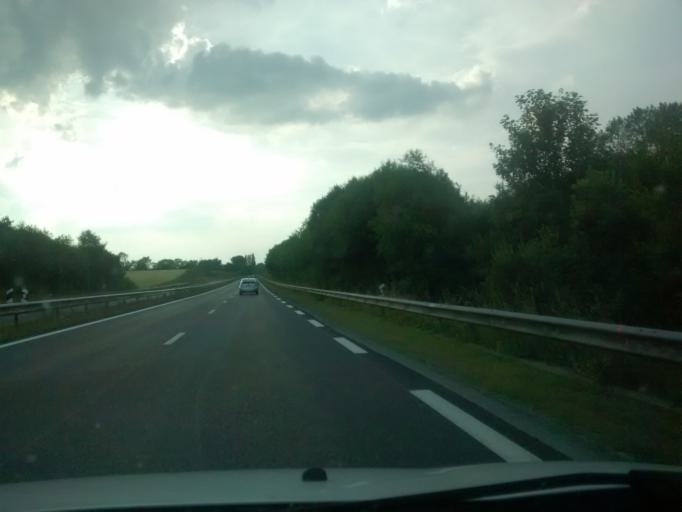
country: FR
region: Brittany
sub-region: Departement des Cotes-d'Armor
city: Pedernec
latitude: 48.5978
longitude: -3.2632
